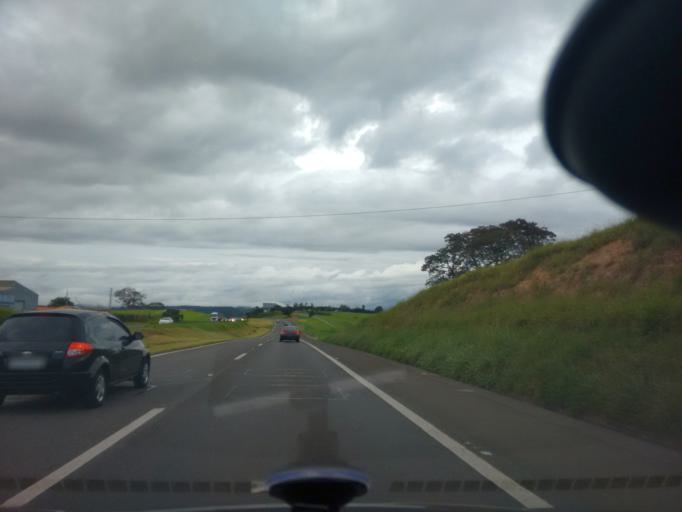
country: BR
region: Sao Paulo
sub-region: Rio Claro
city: Rio Claro
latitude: -22.3422
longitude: -47.6512
